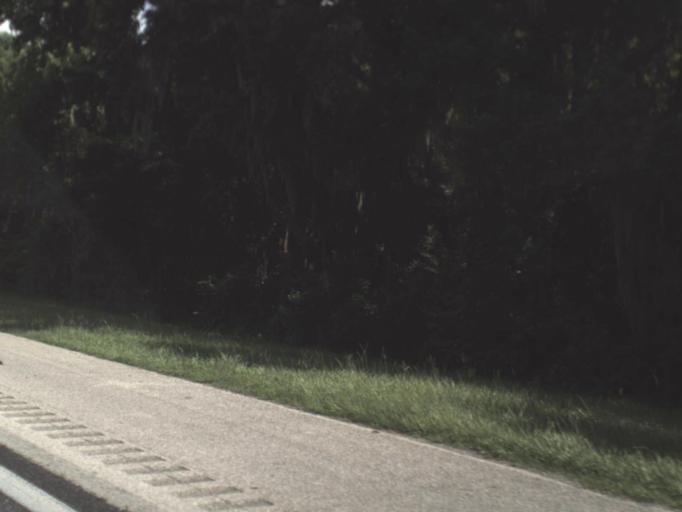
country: US
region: Florida
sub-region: Alachua County
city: Gainesville
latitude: 29.5296
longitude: -82.3155
